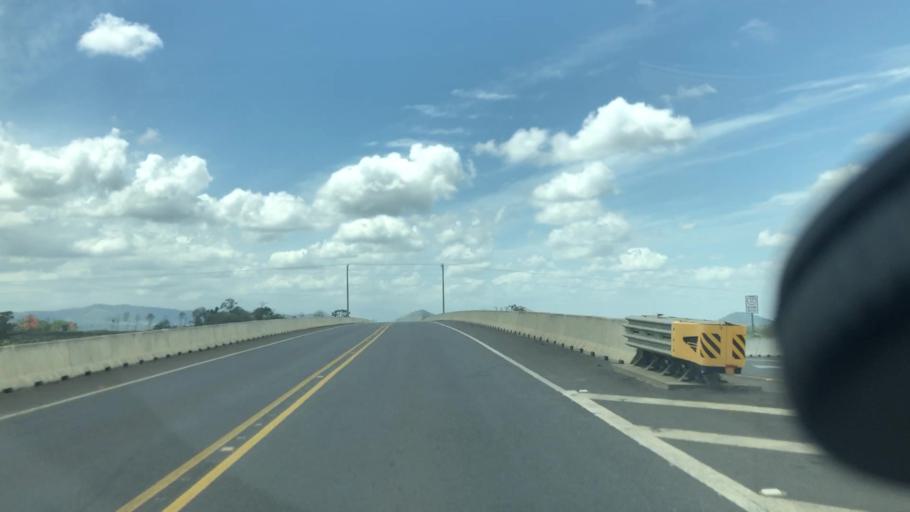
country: CR
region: Alajuela
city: Pital
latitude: 10.4345
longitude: -84.2758
